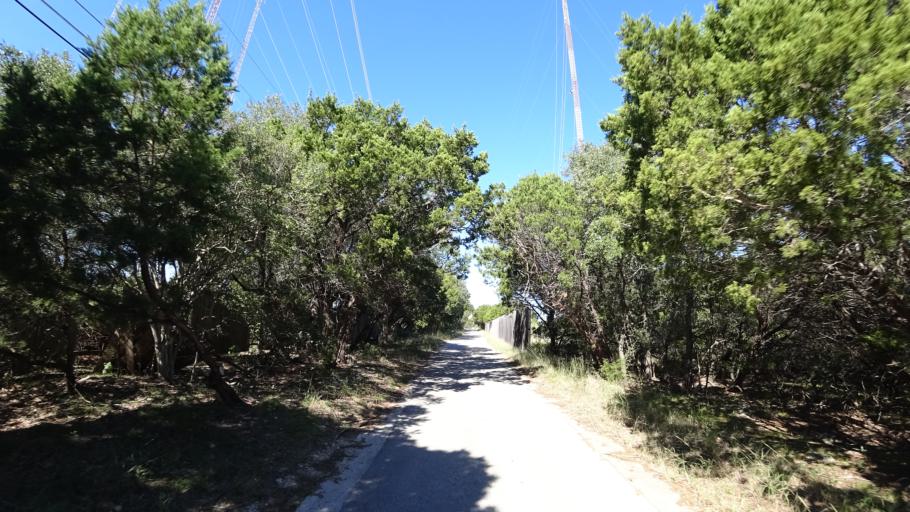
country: US
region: Texas
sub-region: Travis County
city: West Lake Hills
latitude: 30.3237
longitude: -97.7985
